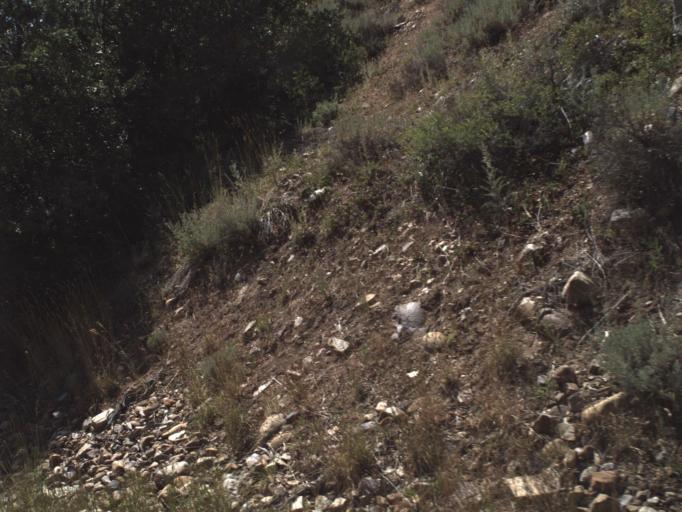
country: US
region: Utah
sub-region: Weber County
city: Wolf Creek
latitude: 41.3344
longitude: -111.6079
